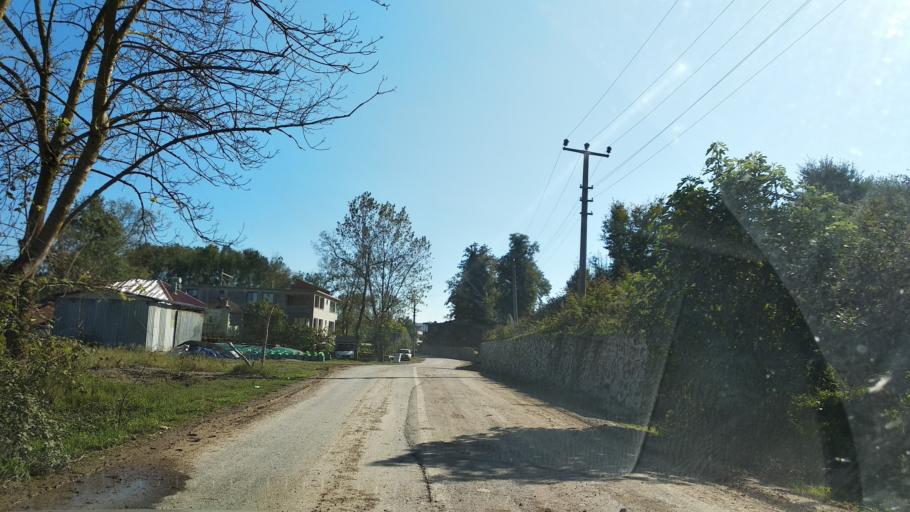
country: TR
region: Sakarya
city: Ortakoy
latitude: 41.0325
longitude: 30.5954
